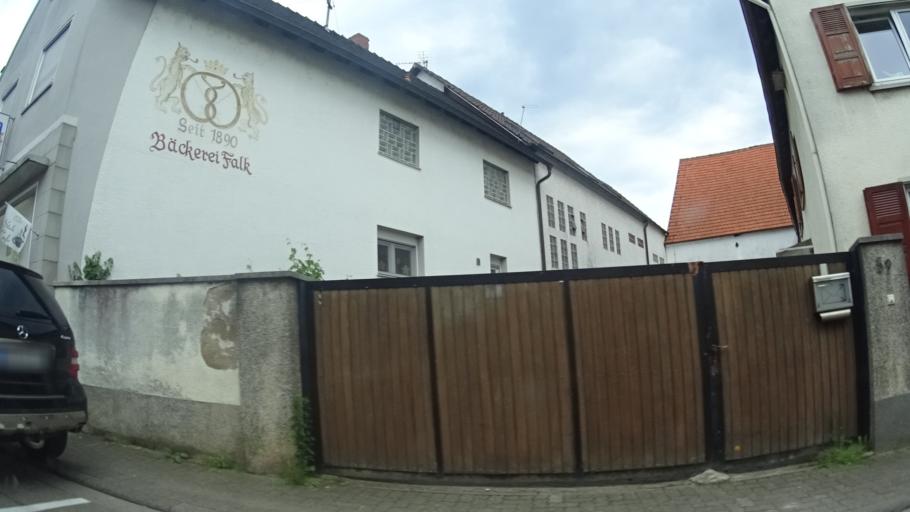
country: DE
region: Rheinland-Pfalz
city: Lustadt
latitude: 49.2449
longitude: 8.2831
